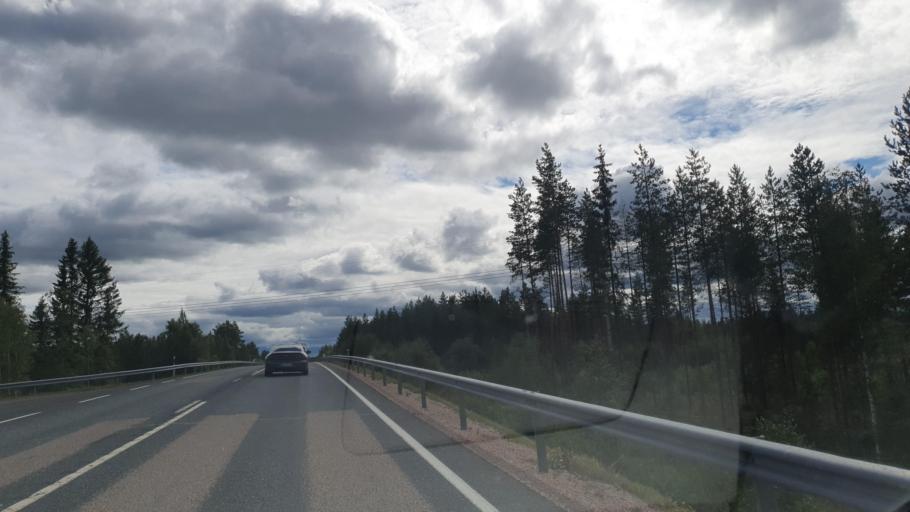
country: FI
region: Kainuu
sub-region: Kajaani
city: Kajaani
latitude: 64.0843
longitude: 27.4528
